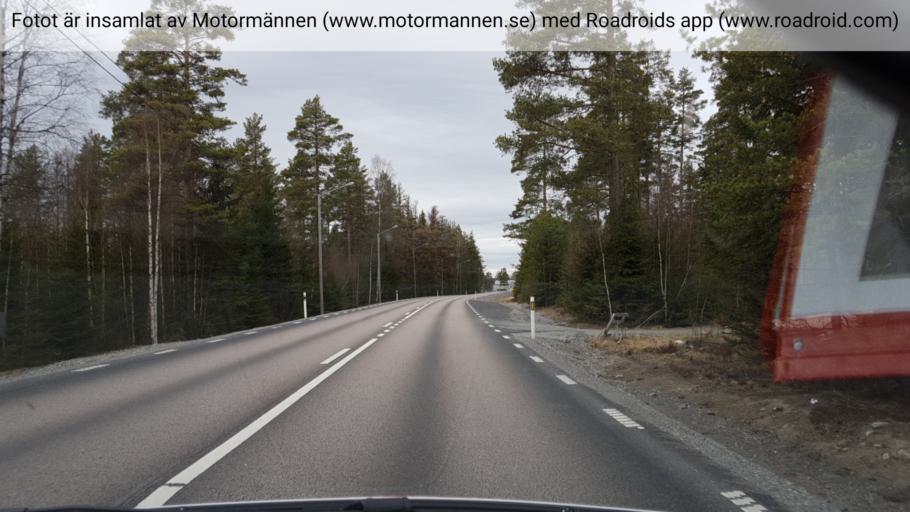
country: SE
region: Vaesternorrland
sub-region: Solleftea Kommun
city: Solleftea
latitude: 63.1524
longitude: 17.3329
